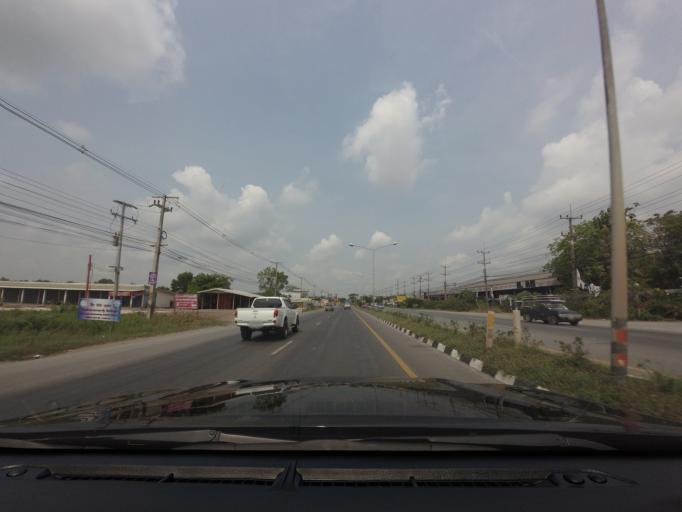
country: TH
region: Nakhon Nayok
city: Ongkharak
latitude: 14.1363
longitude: 100.9886
